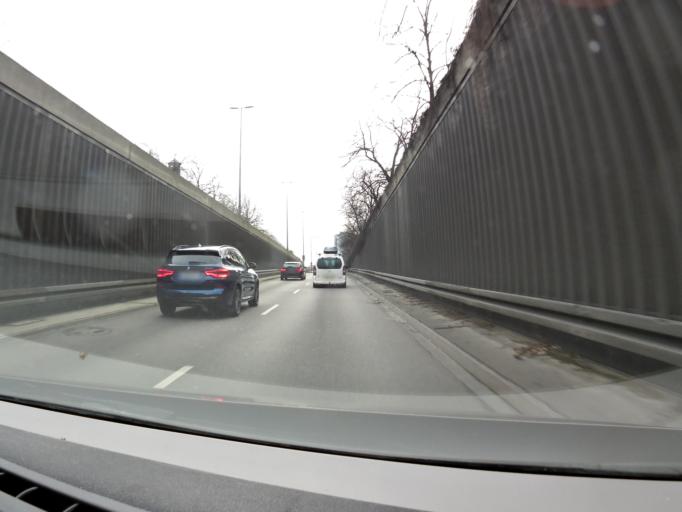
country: DE
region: Bavaria
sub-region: Upper Bavaria
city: Munich
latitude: 48.1519
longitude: 11.5367
